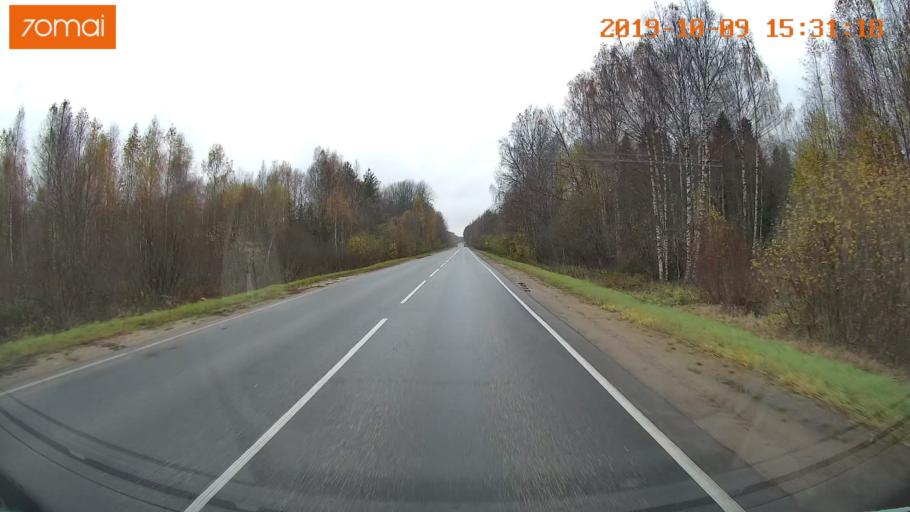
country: RU
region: Kostroma
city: Susanino
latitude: 57.9725
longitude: 41.3057
